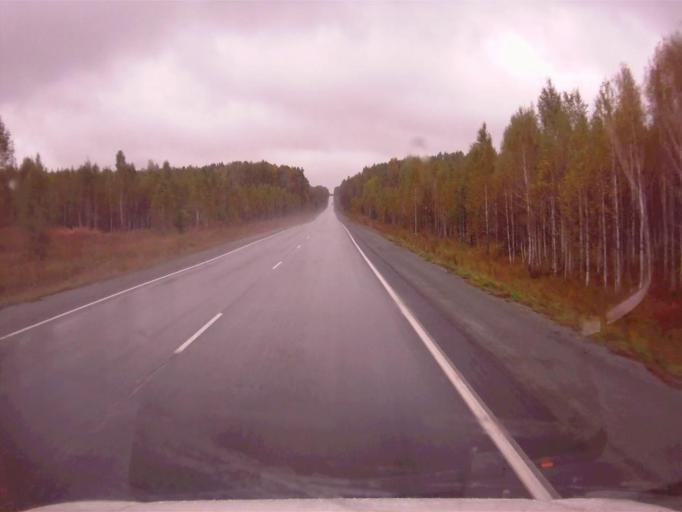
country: RU
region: Chelyabinsk
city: Tayginka
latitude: 55.5153
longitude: 60.6402
